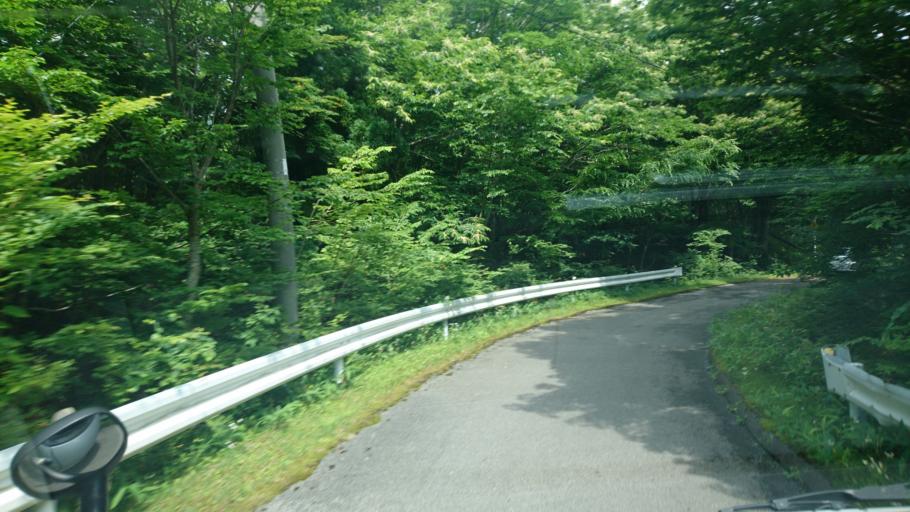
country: JP
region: Iwate
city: Ofunato
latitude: 39.1632
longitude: 141.7484
